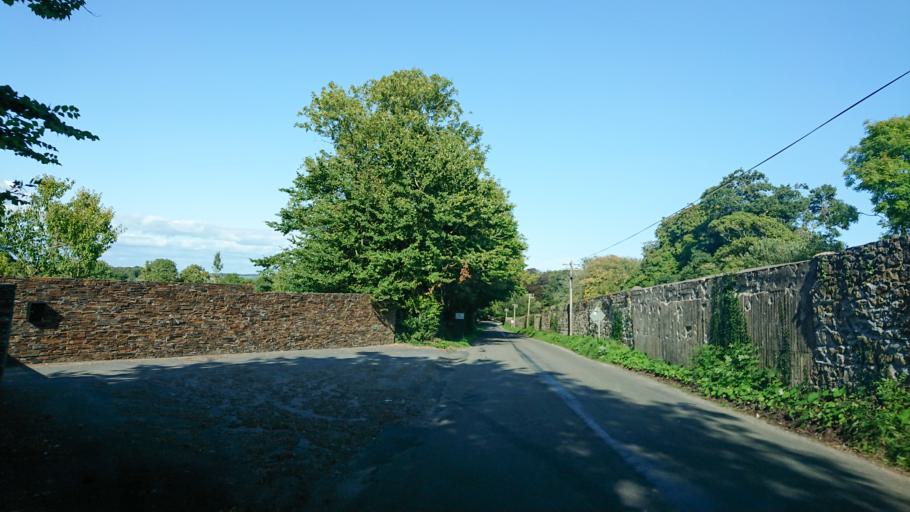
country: IE
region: Munster
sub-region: Waterford
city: Dunmore East
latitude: 52.1905
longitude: -6.9873
